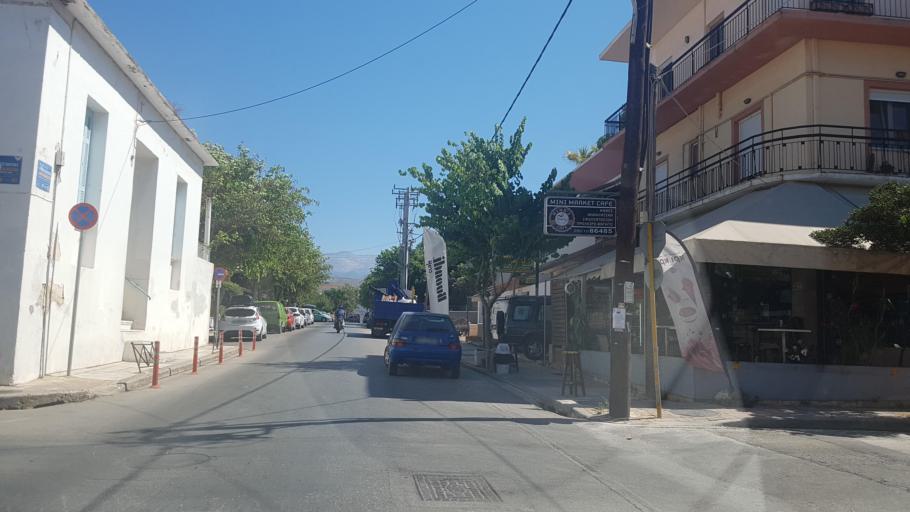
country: GR
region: Crete
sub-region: Nomos Chanias
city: Chania
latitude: 35.5095
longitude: 24.0175
